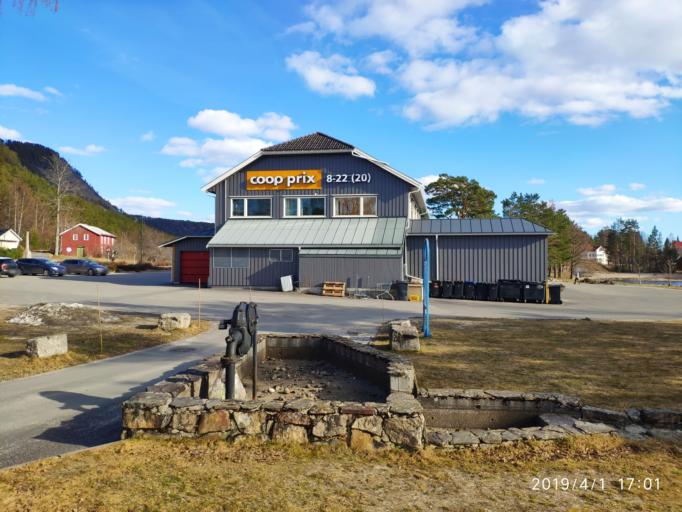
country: NO
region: Telemark
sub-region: Nissedal
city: Treungen
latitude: 59.0193
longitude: 8.5225
